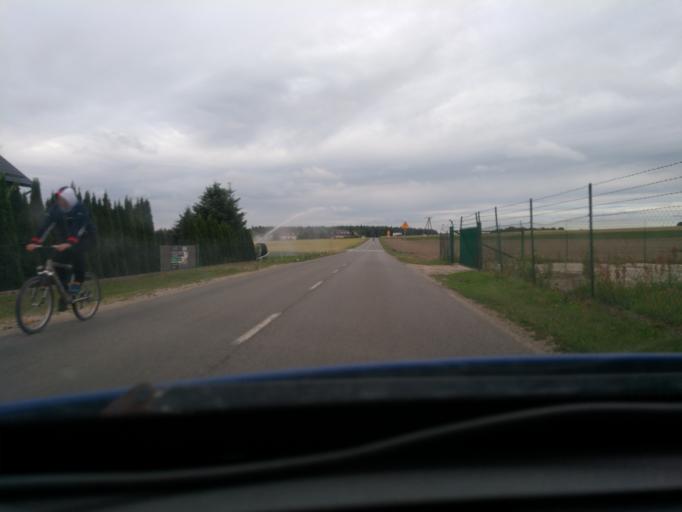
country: PL
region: Pomeranian Voivodeship
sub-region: Powiat kartuski
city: Banino
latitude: 54.3843
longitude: 18.4057
